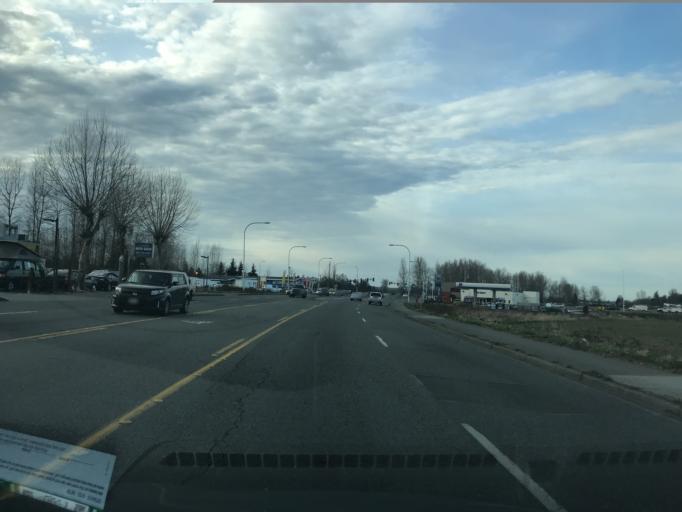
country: US
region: Washington
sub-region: King County
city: Kent
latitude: 47.3518
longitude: -122.2277
